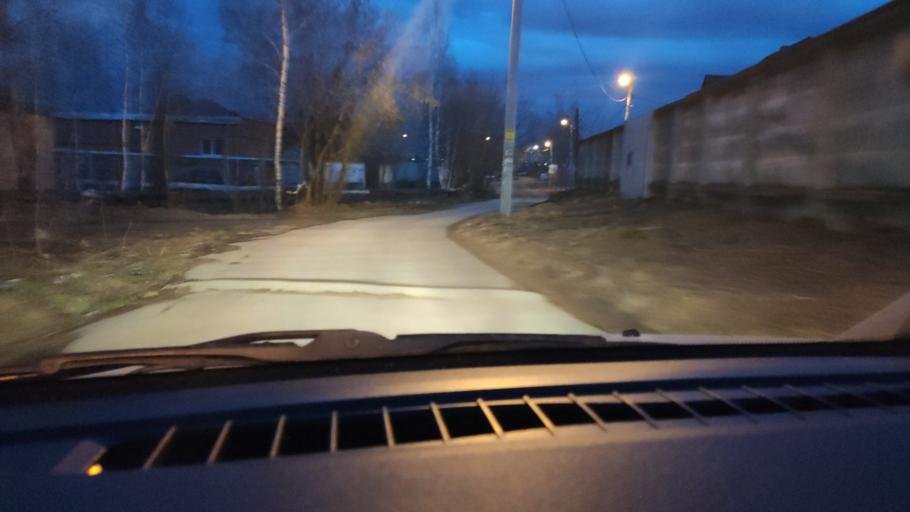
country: RU
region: Perm
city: Perm
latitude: 58.0466
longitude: 56.2858
